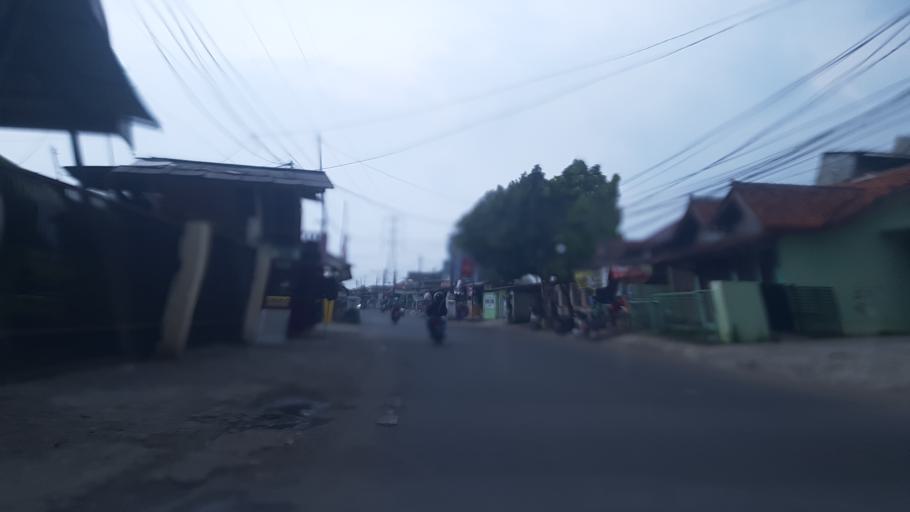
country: ID
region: West Java
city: Cibinong
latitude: -6.5246
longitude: 106.8579
